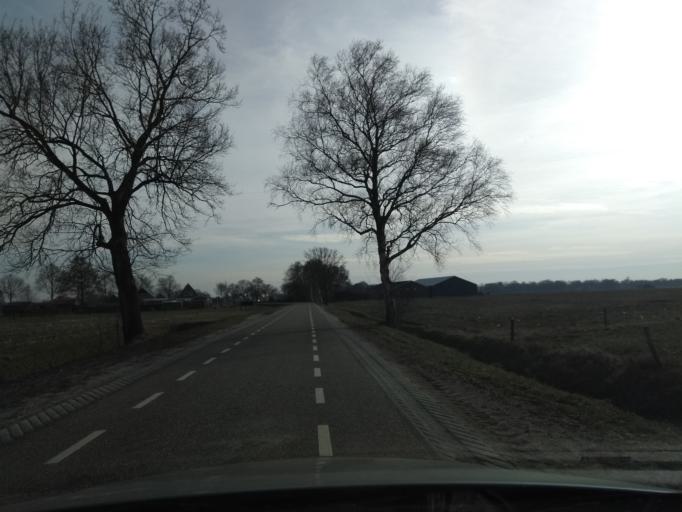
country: NL
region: Overijssel
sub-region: Gemeente Twenterand
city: Vriezenveen
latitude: 52.4310
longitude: 6.6568
